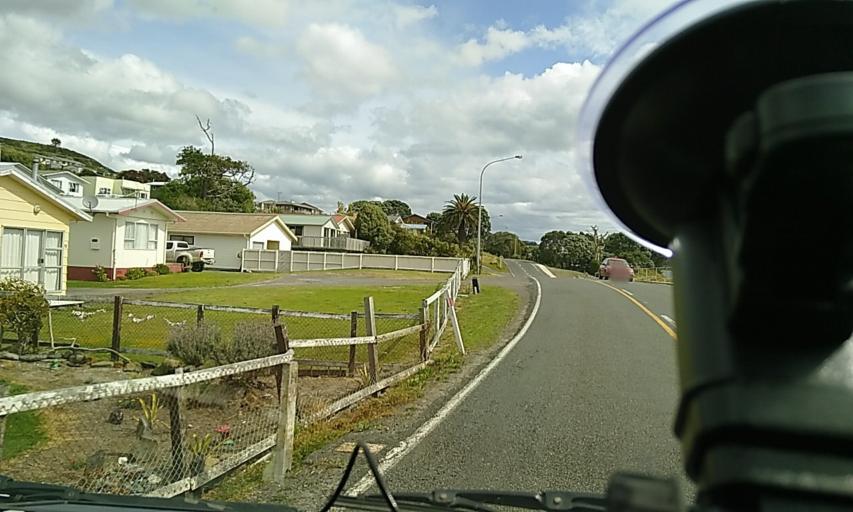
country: NZ
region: Northland
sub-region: Far North District
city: Ahipara
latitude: -35.5110
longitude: 173.3893
